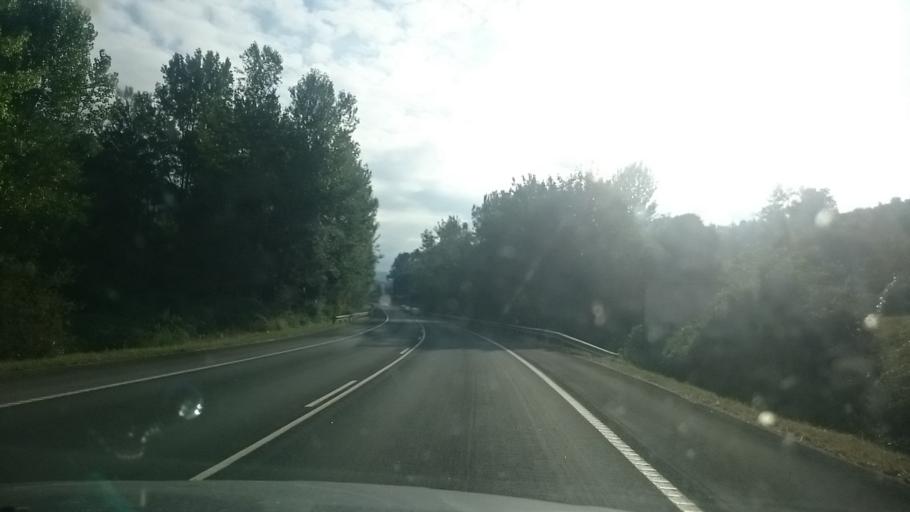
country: ES
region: Asturias
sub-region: Province of Asturias
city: Lugones
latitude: 43.3339
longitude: -5.7657
